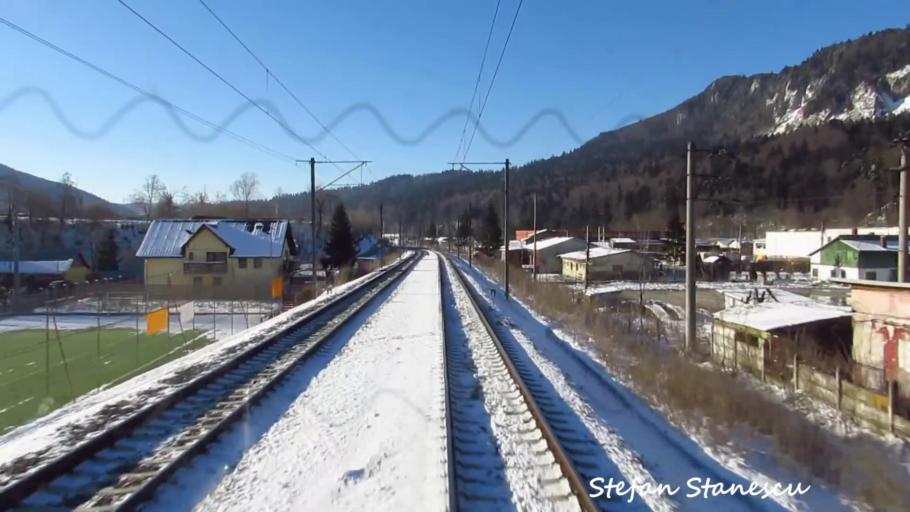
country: RO
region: Prahova
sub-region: Oras Busteni
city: Poiana Tapului
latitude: 45.3813
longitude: 25.5408
